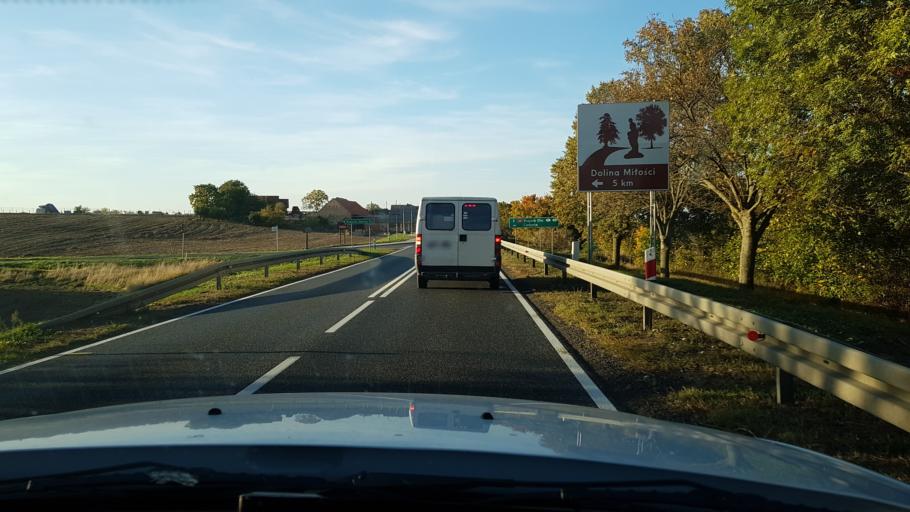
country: DE
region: Brandenburg
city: Schwedt (Oder)
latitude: 53.0247
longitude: 14.3245
